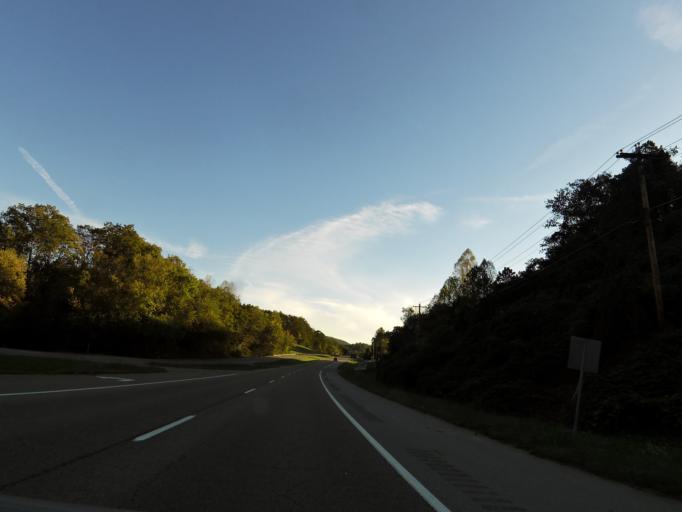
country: US
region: Tennessee
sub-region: Blount County
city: Wildwood
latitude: 35.7248
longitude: -83.8188
